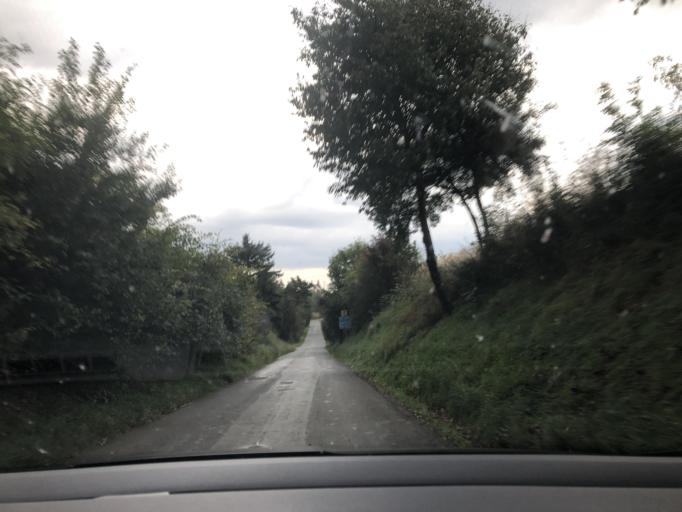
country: CZ
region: Central Bohemia
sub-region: Okres Kolin
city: Tynec nad Labem
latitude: 50.0385
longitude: 15.3662
